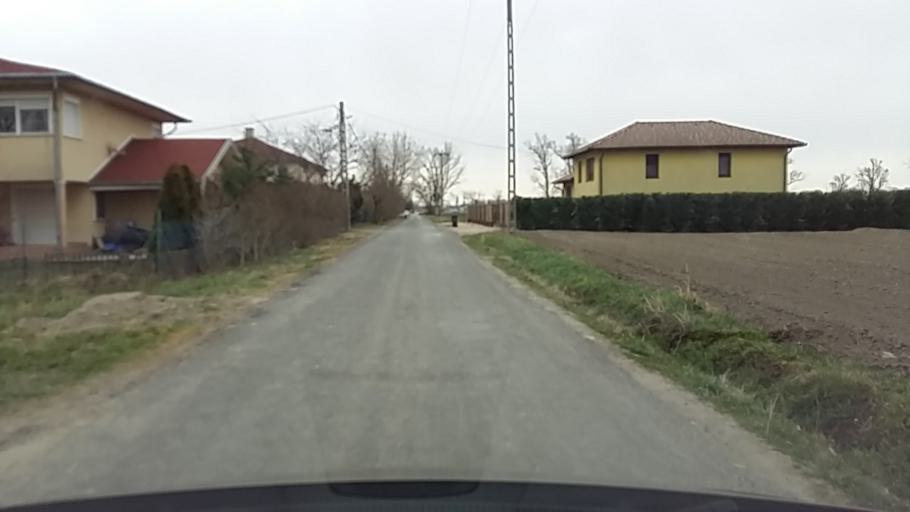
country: HU
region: Pest
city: Szigethalom
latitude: 47.3473
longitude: 19.0137
